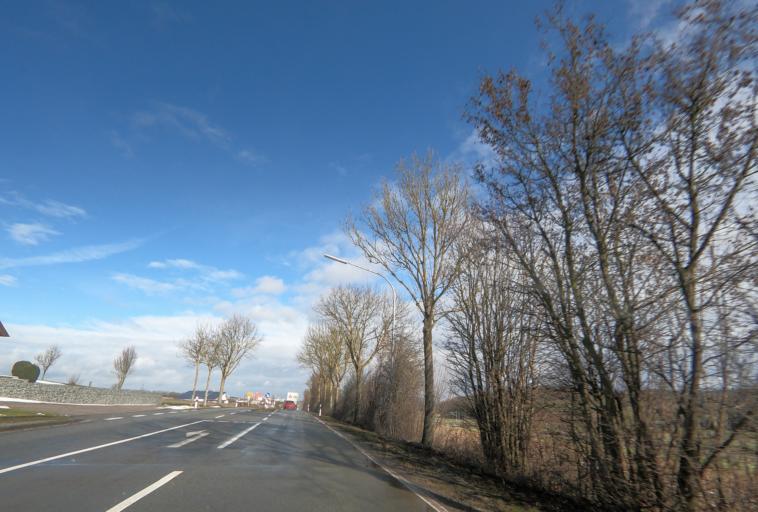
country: DE
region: Bavaria
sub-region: Lower Bavaria
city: Ergoldsbach
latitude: 48.7125
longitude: 12.1924
